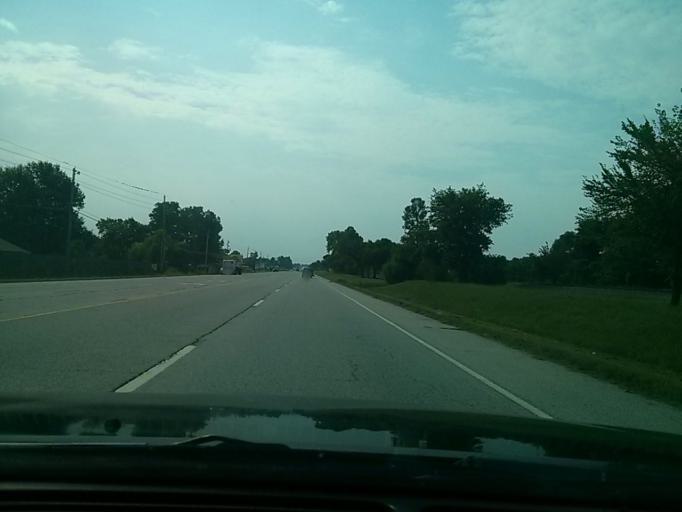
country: US
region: Oklahoma
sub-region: Wagoner County
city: Coweta
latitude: 35.9928
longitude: -95.6743
